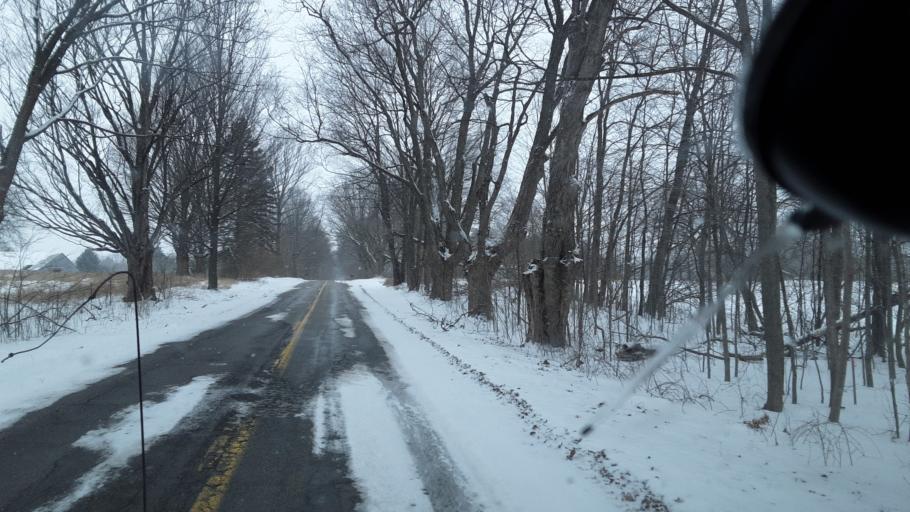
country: US
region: Michigan
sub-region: Ingham County
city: Leslie
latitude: 42.4910
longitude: -84.3730
